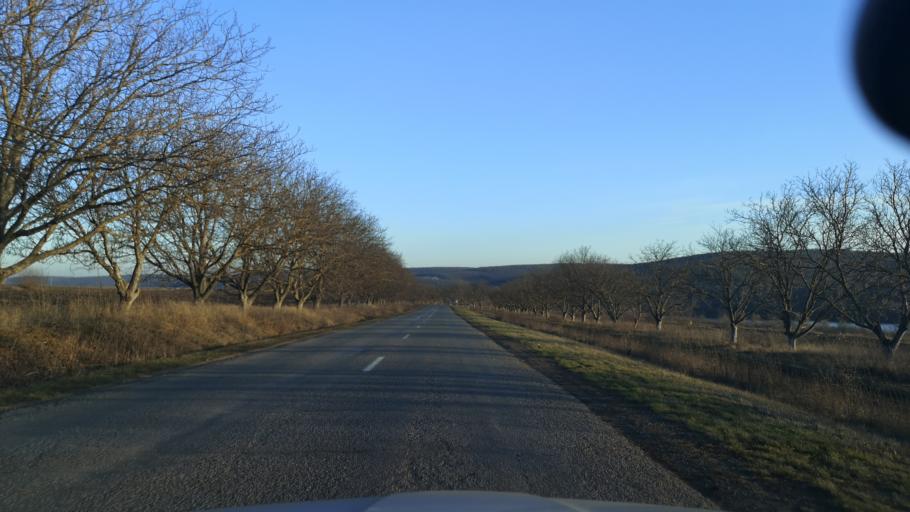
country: MD
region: Orhei
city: Orhei
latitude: 47.2866
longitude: 28.8235
